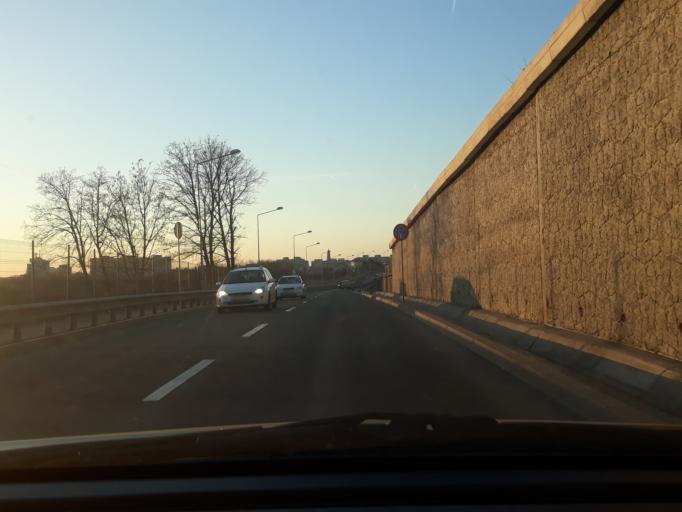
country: RO
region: Bihor
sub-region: Comuna Biharea
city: Oradea
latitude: 47.0543
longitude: 21.9530
